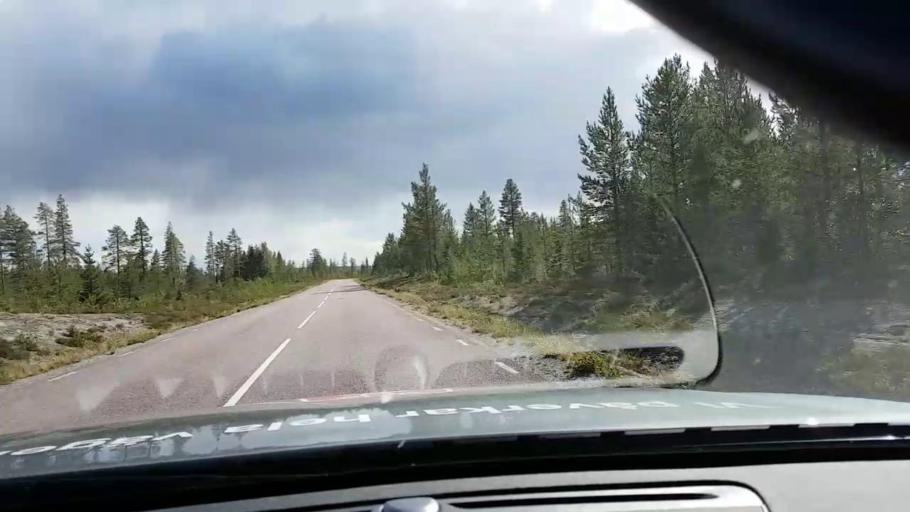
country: SE
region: Vaesterbotten
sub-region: Asele Kommun
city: Asele
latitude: 63.8987
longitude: 17.3490
